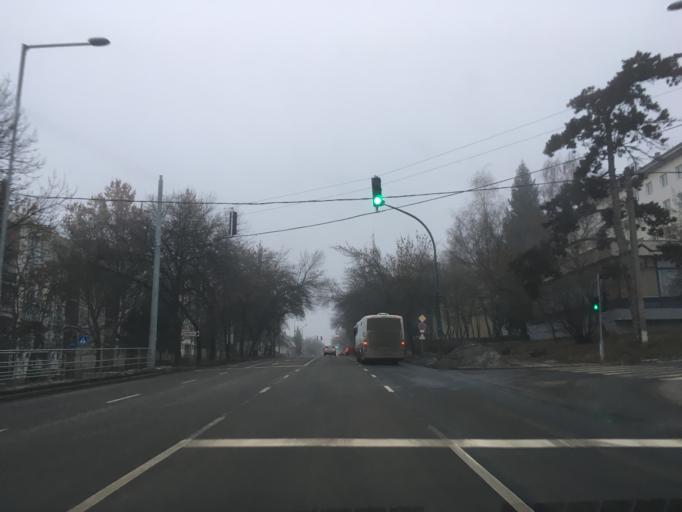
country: HU
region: Heves
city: Eger
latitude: 47.8851
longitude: 20.3809
